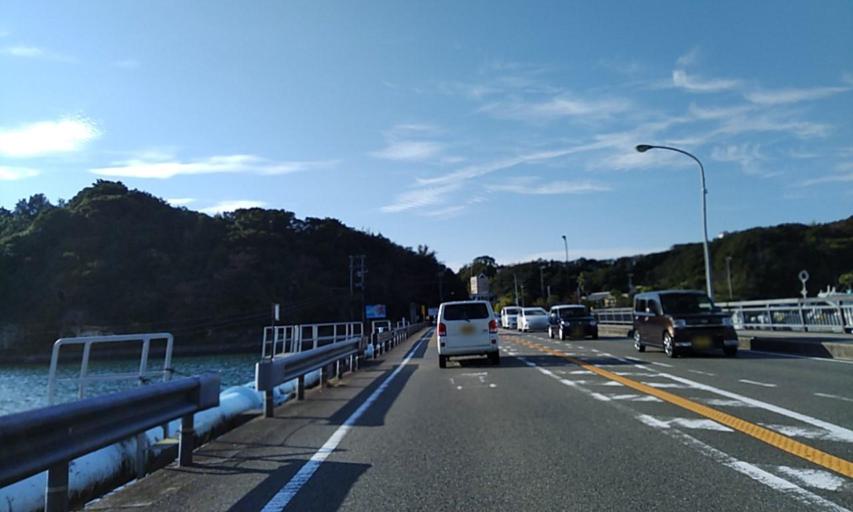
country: JP
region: Wakayama
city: Tanabe
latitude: 33.6796
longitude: 135.3600
